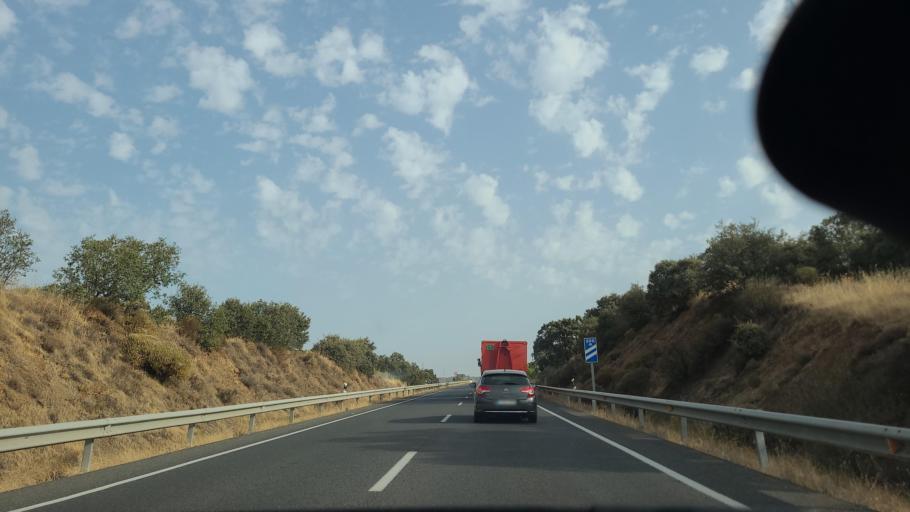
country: ES
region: Andalusia
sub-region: Province of Cordoba
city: Obejo
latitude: 38.0444
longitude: -4.8084
